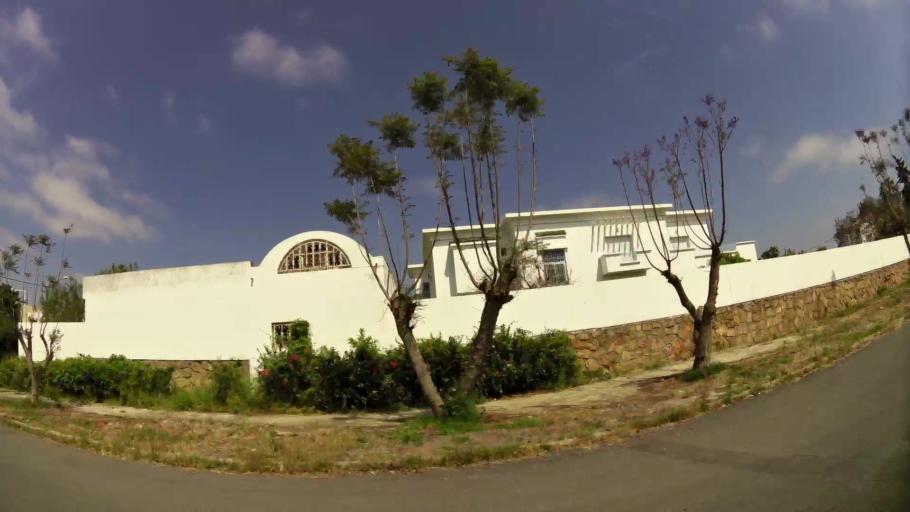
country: MA
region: Rabat-Sale-Zemmour-Zaer
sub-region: Rabat
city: Rabat
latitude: 33.9858
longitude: -6.8309
